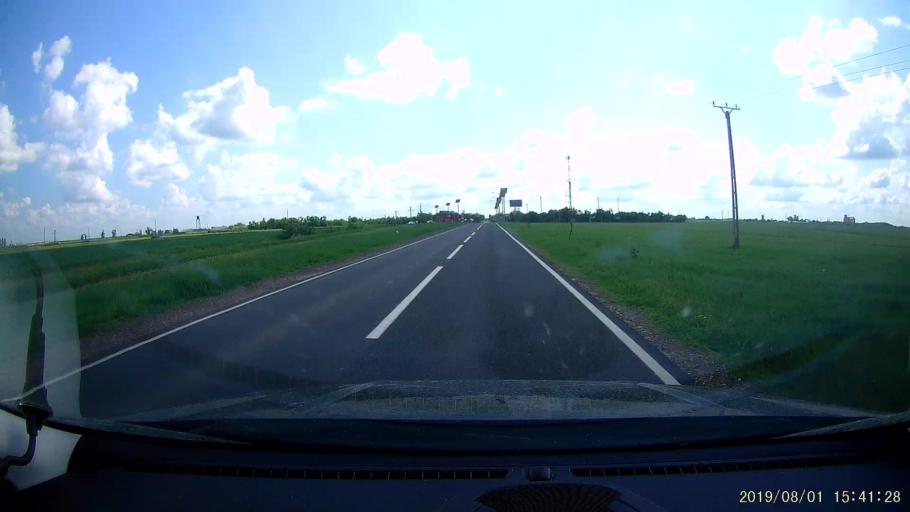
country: RO
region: Braila
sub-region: Comuna Baraganul
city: Baraganul
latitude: 44.8221
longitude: 27.5257
